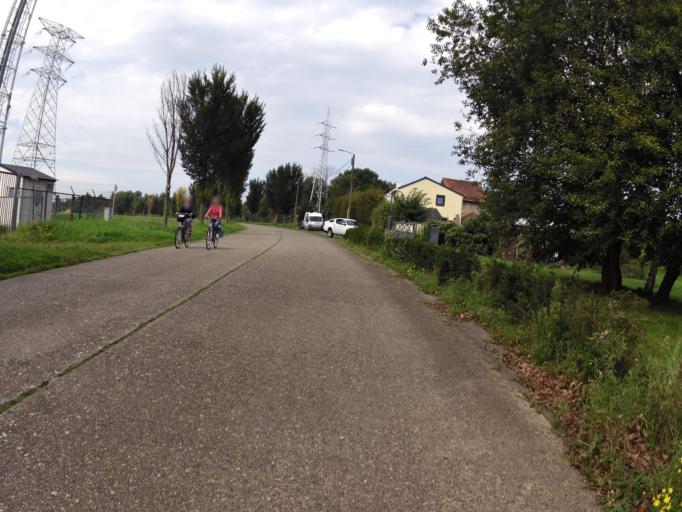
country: BE
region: Flanders
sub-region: Provincie Limburg
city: Lanaken
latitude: 50.8839
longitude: 5.6457
